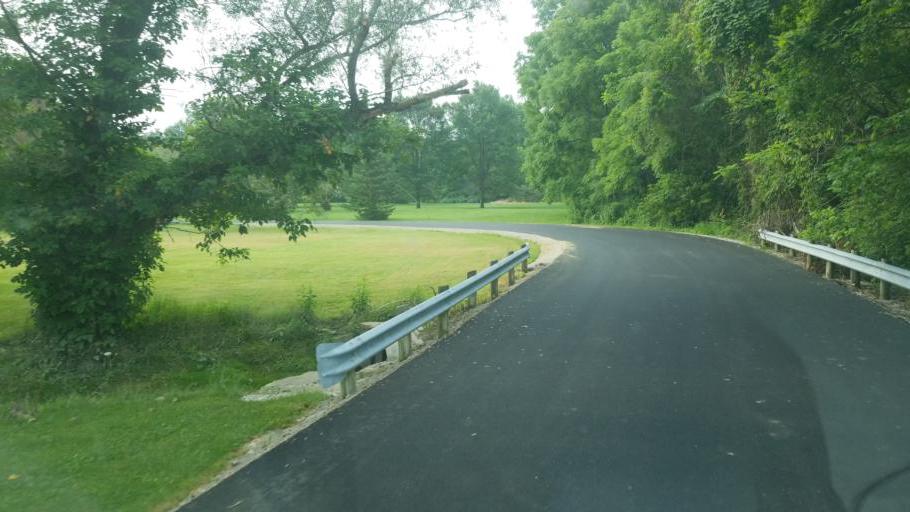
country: US
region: Ohio
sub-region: Morrow County
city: Cardington
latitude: 40.5042
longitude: -82.9059
